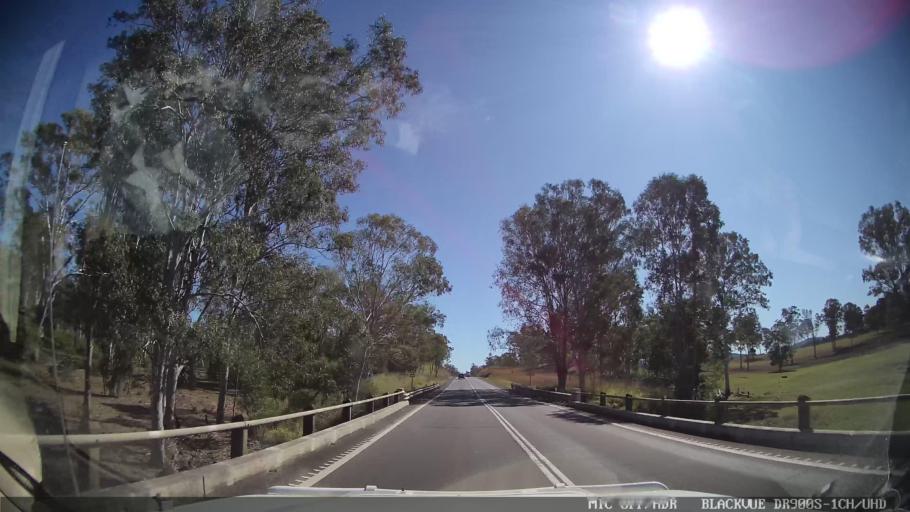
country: AU
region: Queensland
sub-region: Gympie Regional Council
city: Gympie
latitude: -26.0393
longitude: 152.5701
